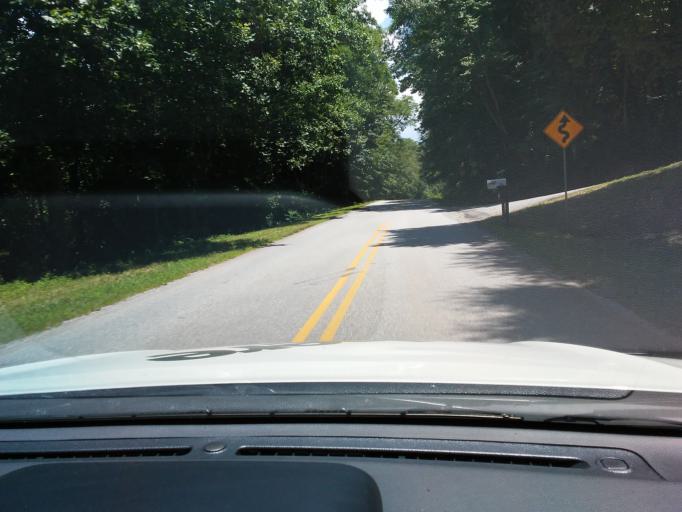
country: US
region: Georgia
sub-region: Towns County
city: Hiawassee
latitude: 34.8699
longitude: -83.7296
